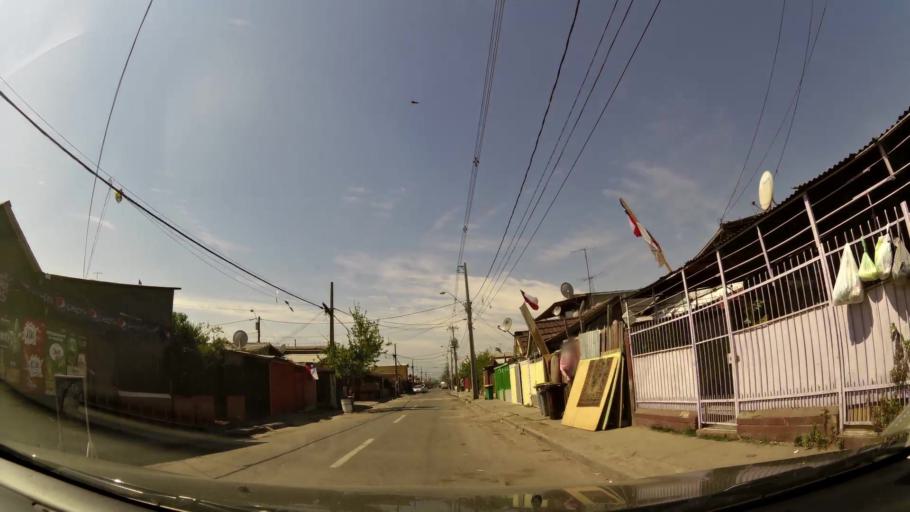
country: CL
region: Santiago Metropolitan
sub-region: Provincia de Santiago
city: La Pintana
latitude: -33.5904
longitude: -70.6269
